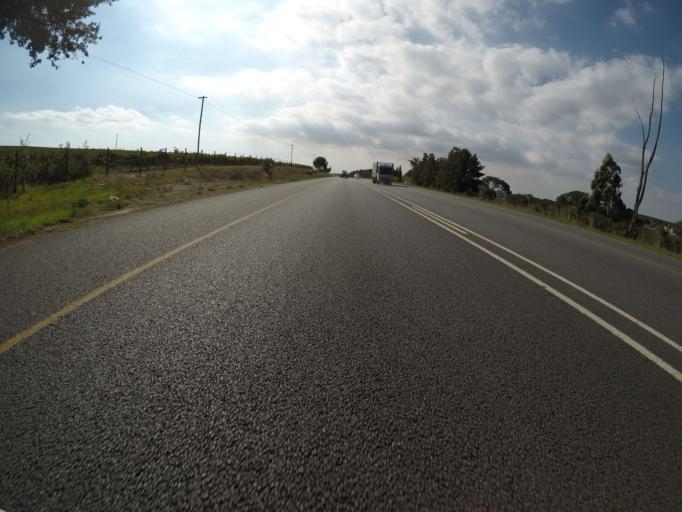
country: ZA
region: Western Cape
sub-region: Cape Winelands District Municipality
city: Stellenbosch
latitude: -33.8831
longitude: 18.8192
